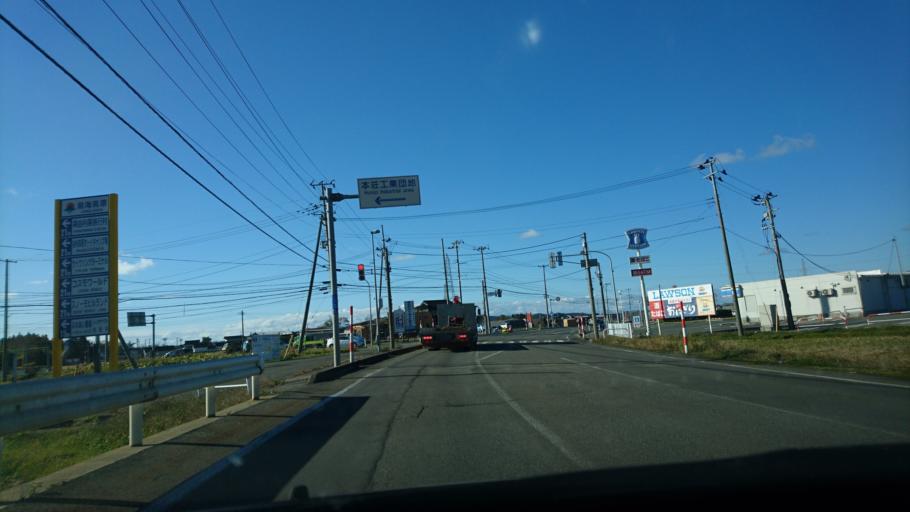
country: JP
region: Akita
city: Akita
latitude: 39.3546
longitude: 140.0821
